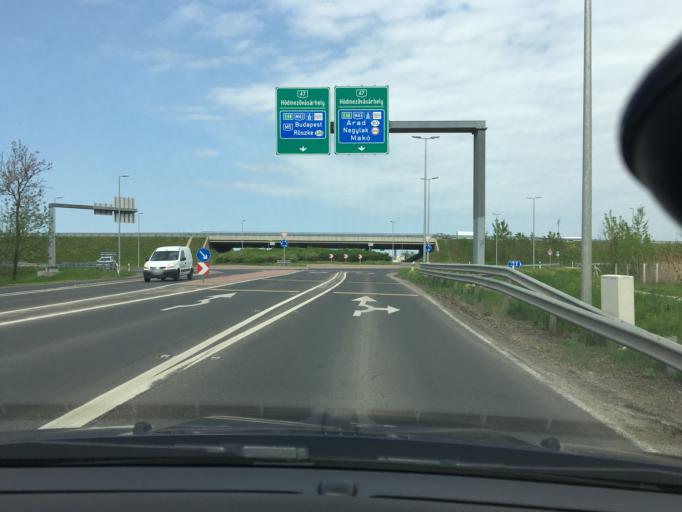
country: HU
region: Csongrad
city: Szeged
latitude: 46.2936
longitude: 20.1759
